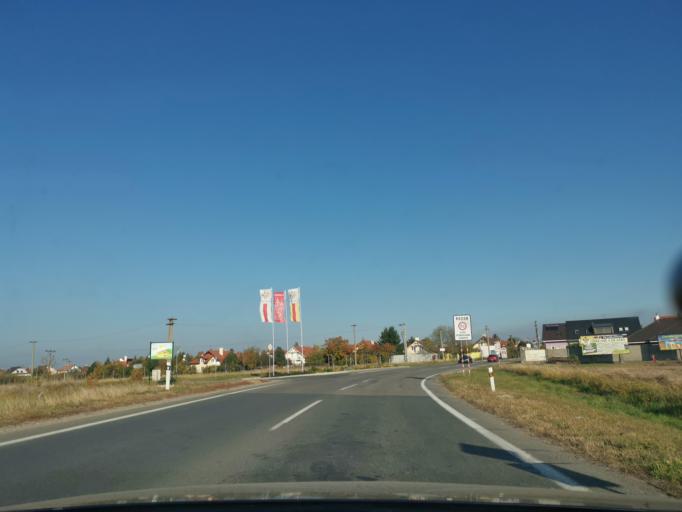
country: SK
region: Bratislavsky
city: Stupava
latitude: 48.3295
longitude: 17.0317
